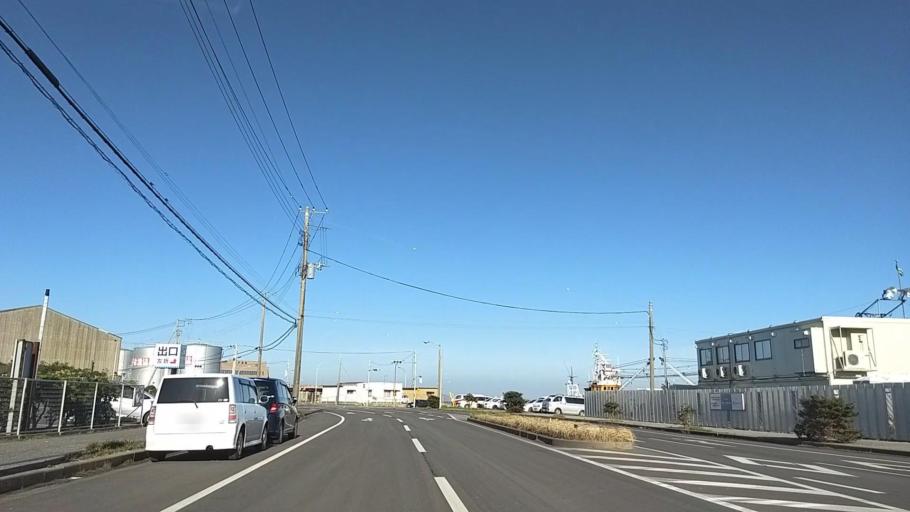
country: JP
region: Chiba
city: Hasaki
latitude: 35.7410
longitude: 140.8646
